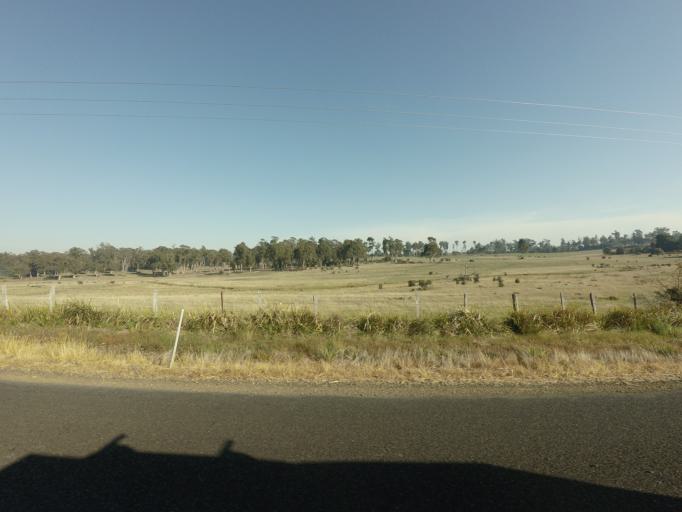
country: AU
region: Tasmania
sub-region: Northern Midlands
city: Longford
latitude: -41.5466
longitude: 146.9919
